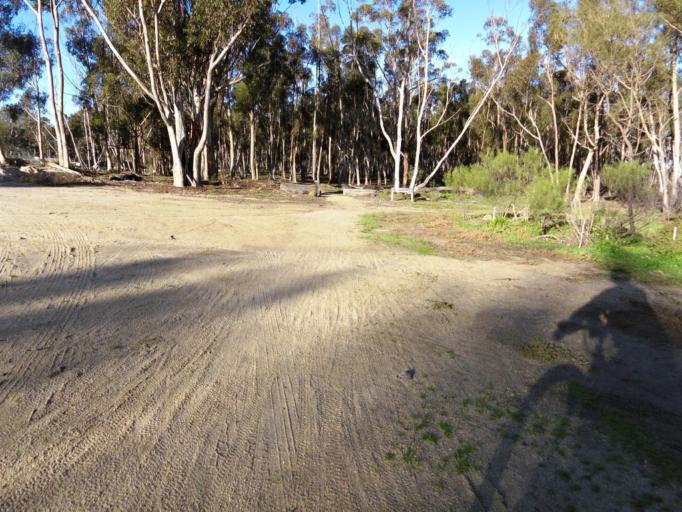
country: AU
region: Victoria
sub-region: Greater Geelong
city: Lara
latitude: -37.9646
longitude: 144.4094
